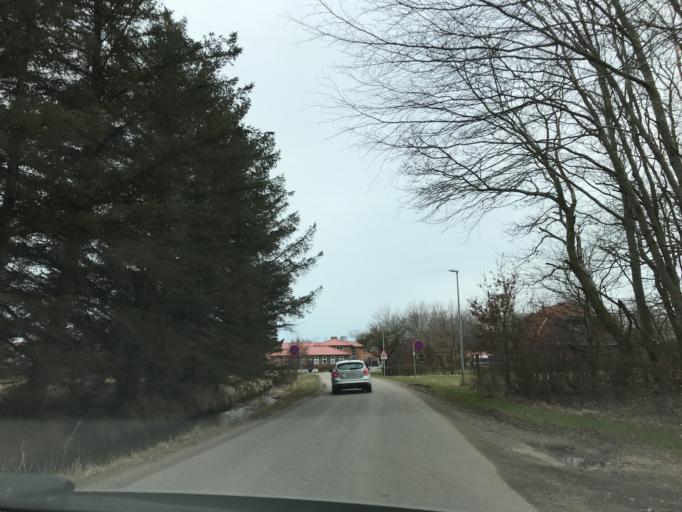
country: DK
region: South Denmark
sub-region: Varde Kommune
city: Oksbol
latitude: 55.8111
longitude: 8.2984
